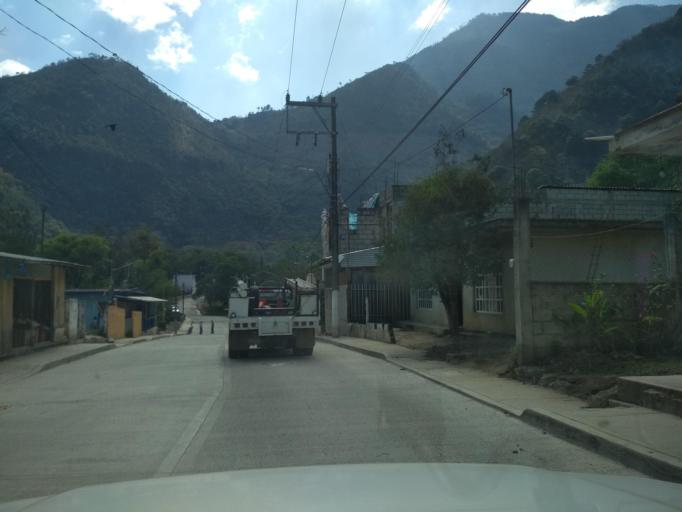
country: MX
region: Veracruz
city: Jalapilla
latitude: 18.8032
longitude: -97.1036
